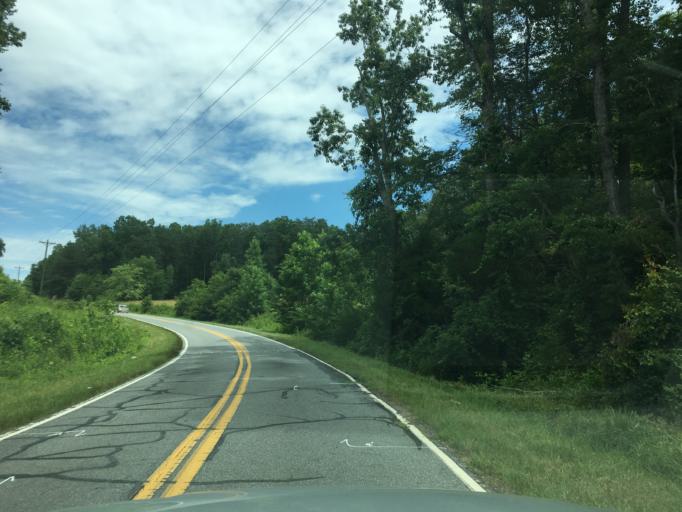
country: US
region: North Carolina
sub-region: Rutherford County
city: Rutherfordton
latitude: 35.2942
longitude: -82.0041
